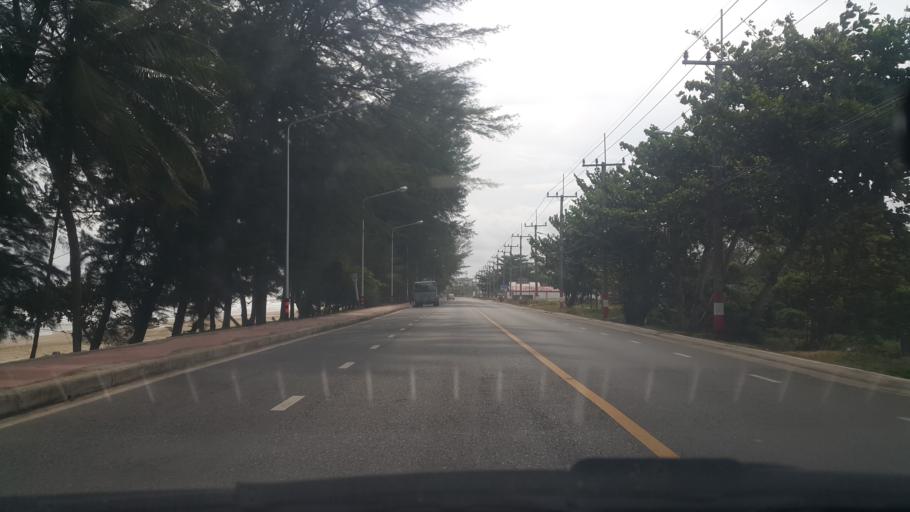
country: TH
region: Rayong
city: Rayong
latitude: 12.6203
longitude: 101.3681
